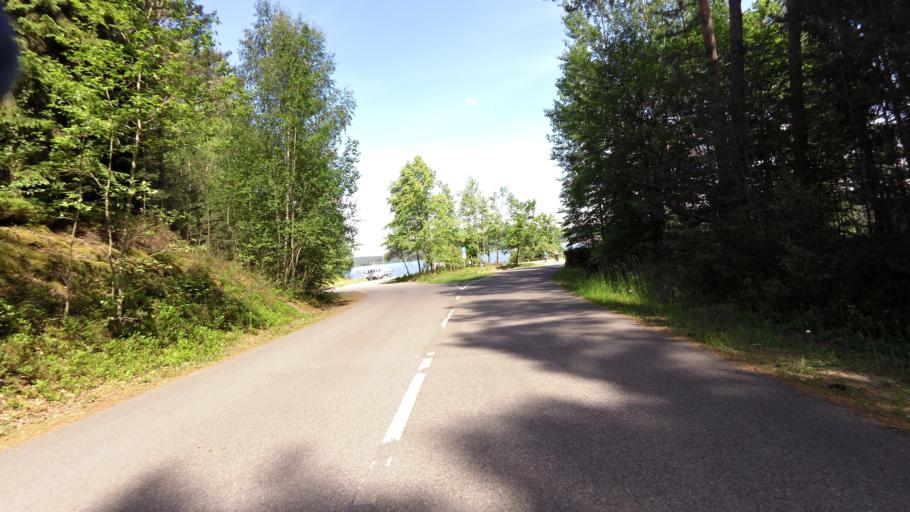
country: DE
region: Bavaria
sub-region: Regierungsbezirk Mittelfranken
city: Pleinfeld
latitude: 49.1189
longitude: 10.9650
